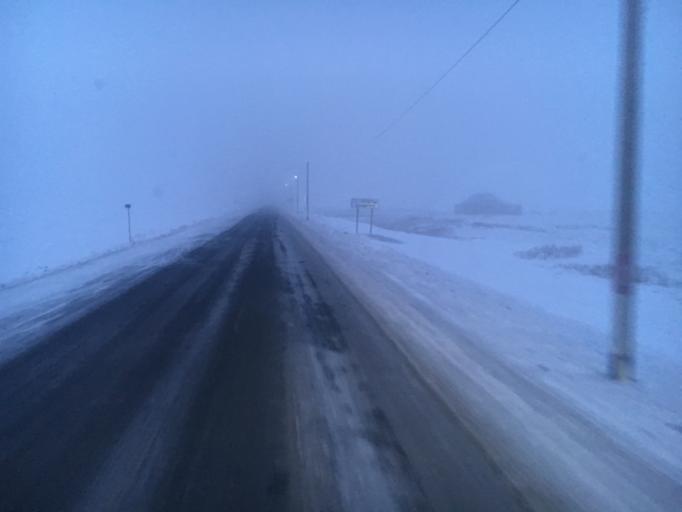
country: KZ
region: Batys Qazaqstan
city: Dzhambeyty
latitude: 50.2577
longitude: 52.6289
